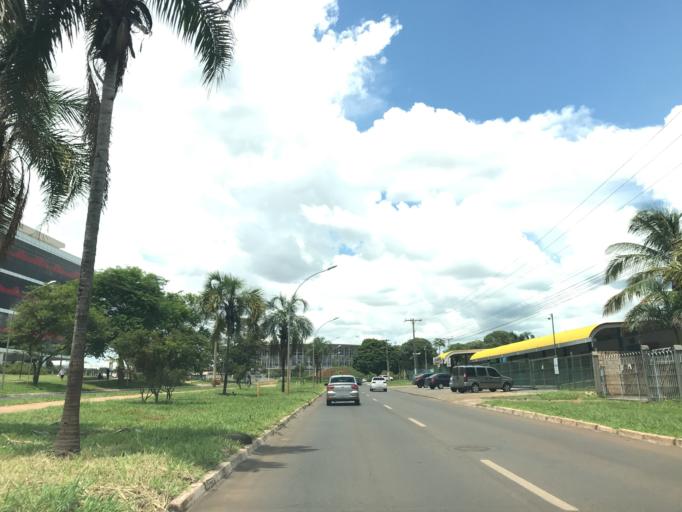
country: BR
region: Federal District
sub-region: Brasilia
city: Brasilia
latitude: -15.7832
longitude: -47.8890
